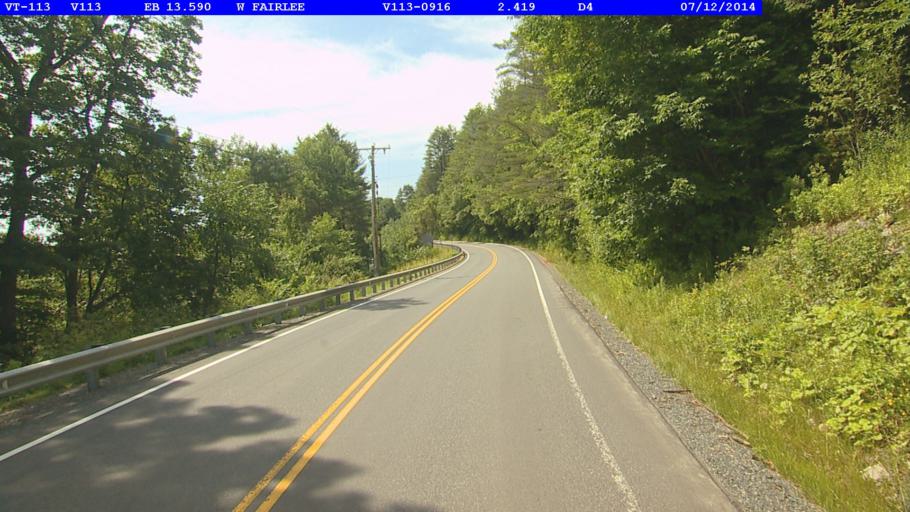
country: US
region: New Hampshire
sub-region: Grafton County
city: Orford
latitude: 43.9028
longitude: -72.2631
